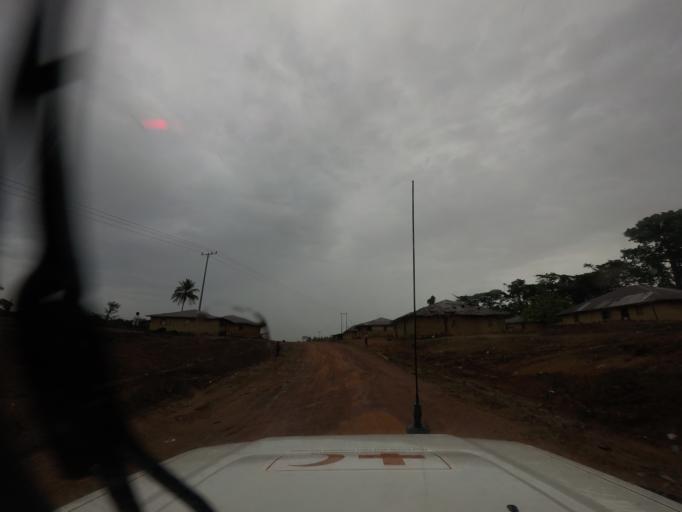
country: LR
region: Nimba
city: Sanniquellie
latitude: 7.2301
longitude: -8.8930
